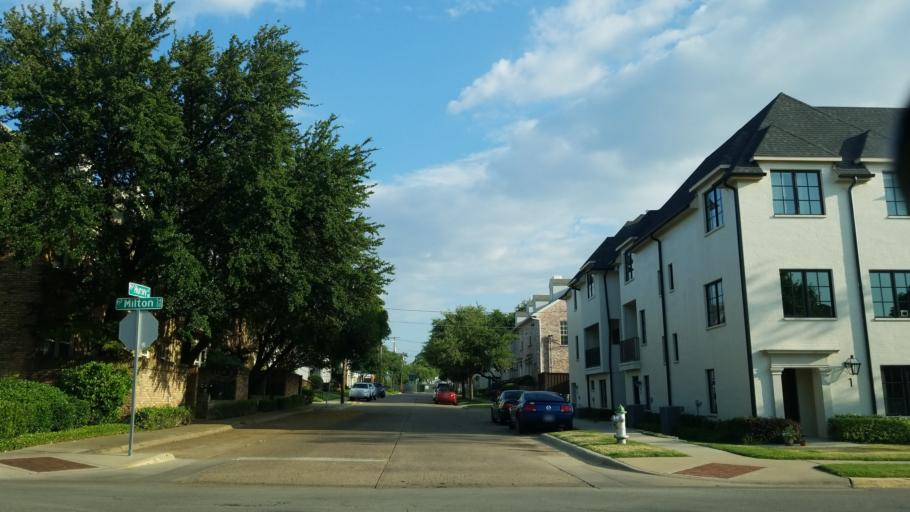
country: US
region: Texas
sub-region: Dallas County
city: University Park
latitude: 32.8486
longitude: -96.7892
